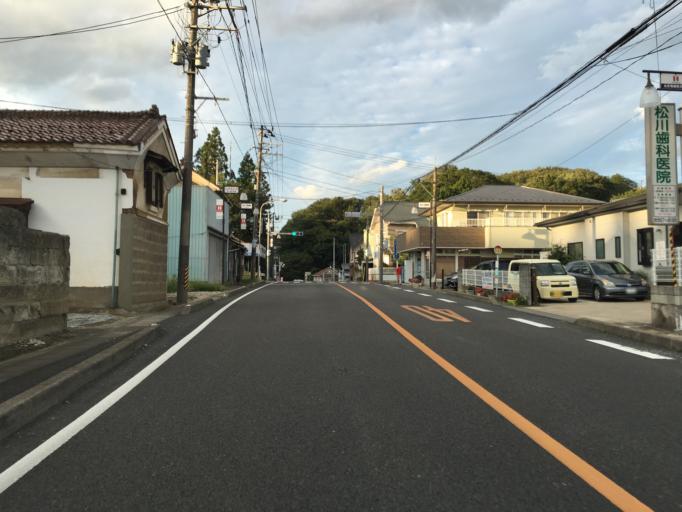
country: JP
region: Fukushima
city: Nihommatsu
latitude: 37.6594
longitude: 140.4613
